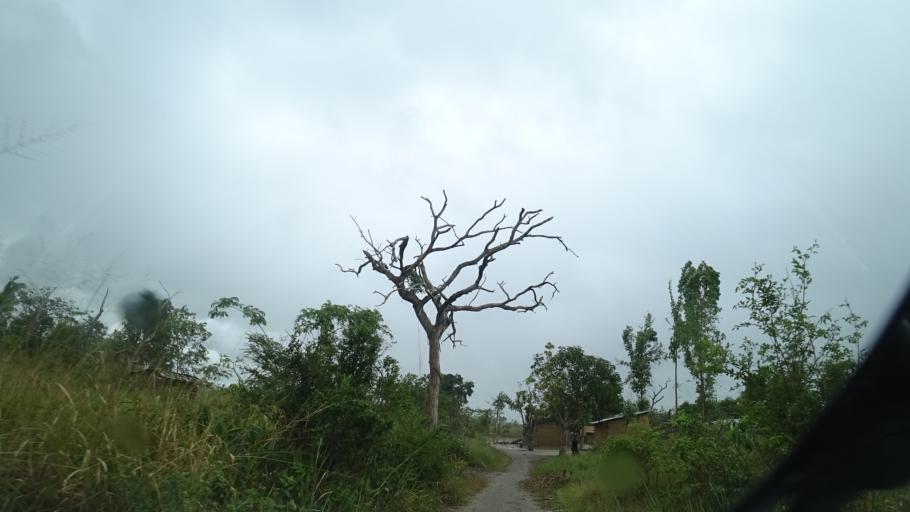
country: MZ
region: Sofala
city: Dondo
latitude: -19.5505
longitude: 35.0531
